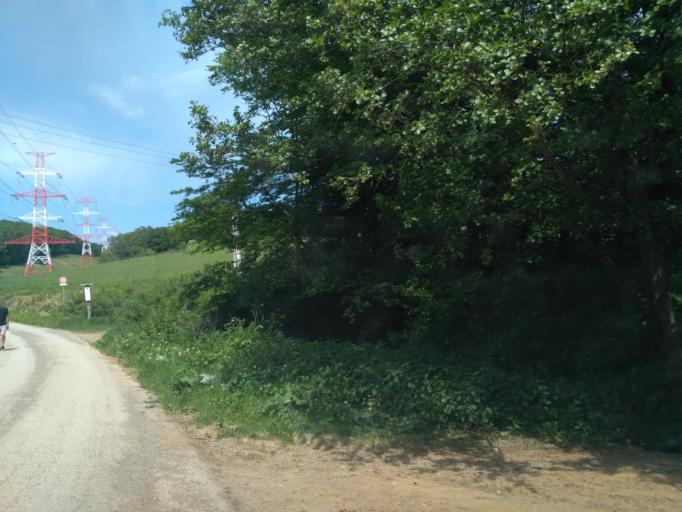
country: SK
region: Kosicky
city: Kosice
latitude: 48.7323
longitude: 21.1861
